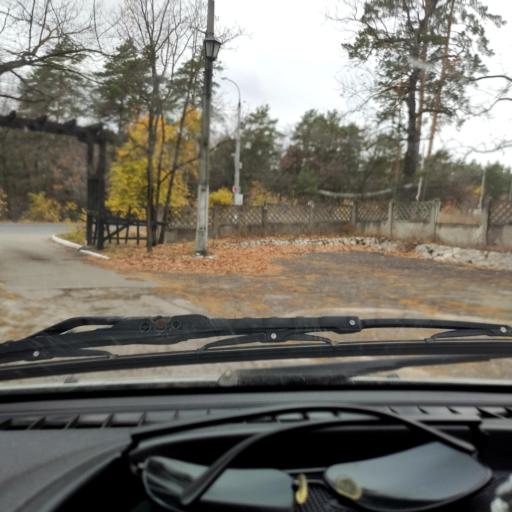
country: RU
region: Samara
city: Tol'yatti
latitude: 53.4860
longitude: 49.3147
